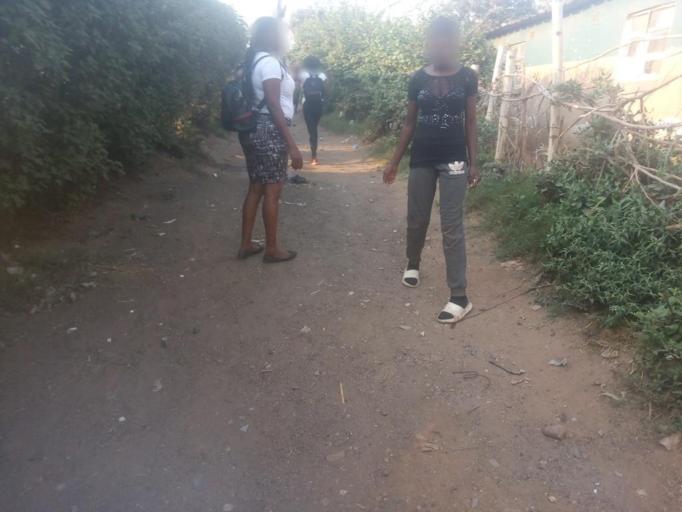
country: ZM
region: Lusaka
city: Lusaka
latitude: -15.4061
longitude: 28.3667
